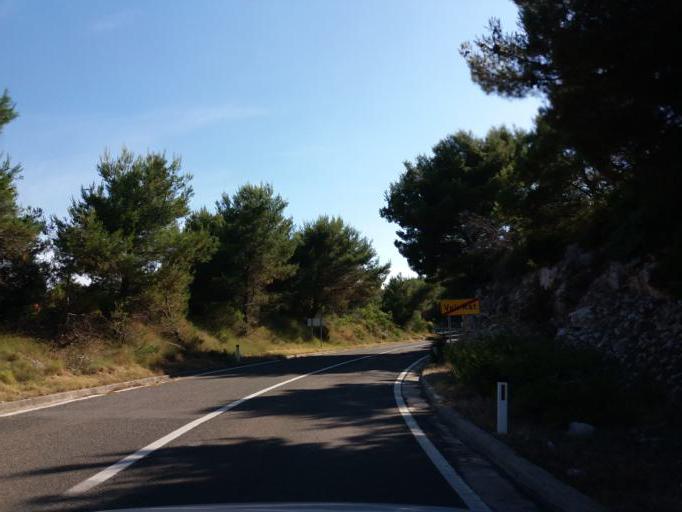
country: HR
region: Zadarska
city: Ugljan
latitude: 44.1380
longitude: 14.8551
